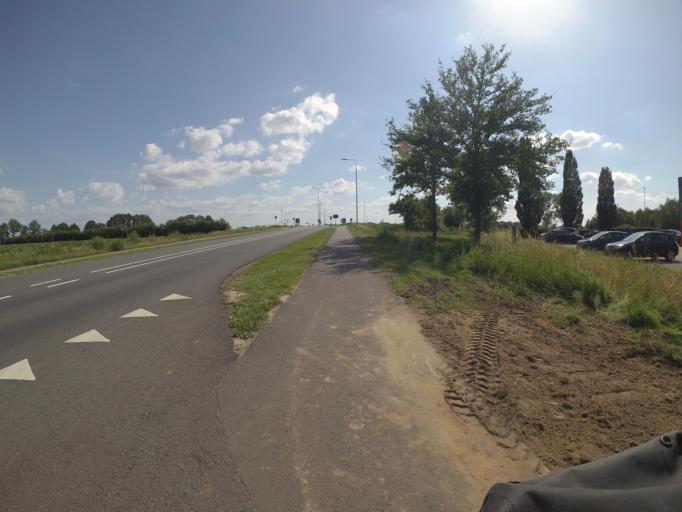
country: NL
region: North Brabant
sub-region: Gemeente Sint-Michielsgestel
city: Sint-Michielsgestel
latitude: 51.6741
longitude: 5.3920
